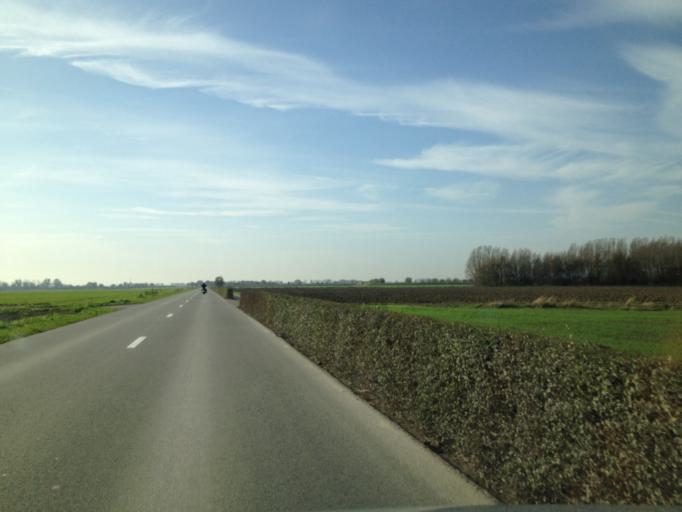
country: NL
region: Zeeland
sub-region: Gemeente Sluis
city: Sluis
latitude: 51.3429
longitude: 3.3760
